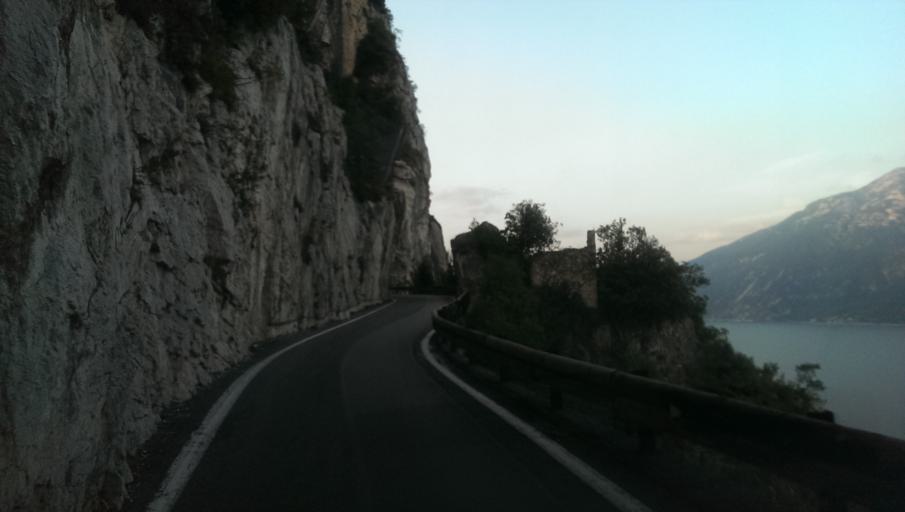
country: IT
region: Lombardy
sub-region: Provincia di Brescia
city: Pieve
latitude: 45.7713
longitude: 10.7651
